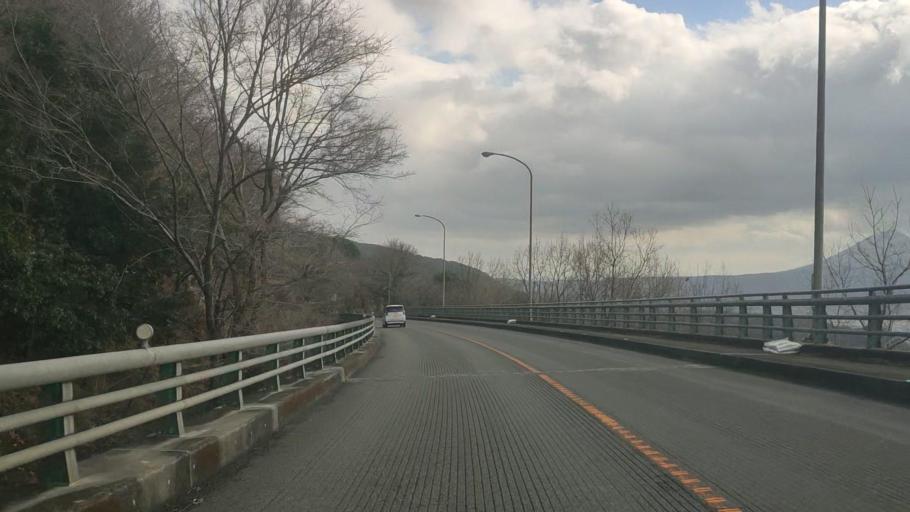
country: JP
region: Kumamoto
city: Hitoyoshi
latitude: 32.0711
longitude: 130.7978
